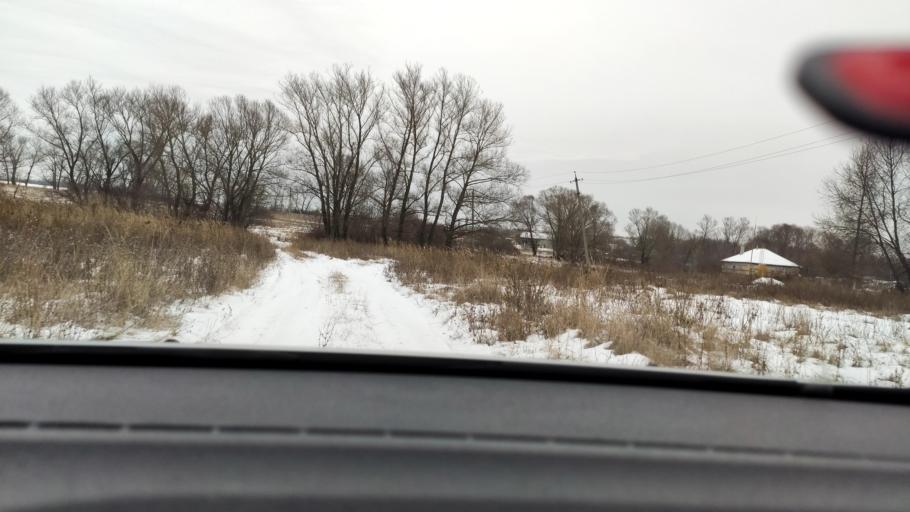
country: RU
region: Voronezj
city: Semiluki
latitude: 51.7025
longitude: 38.9718
